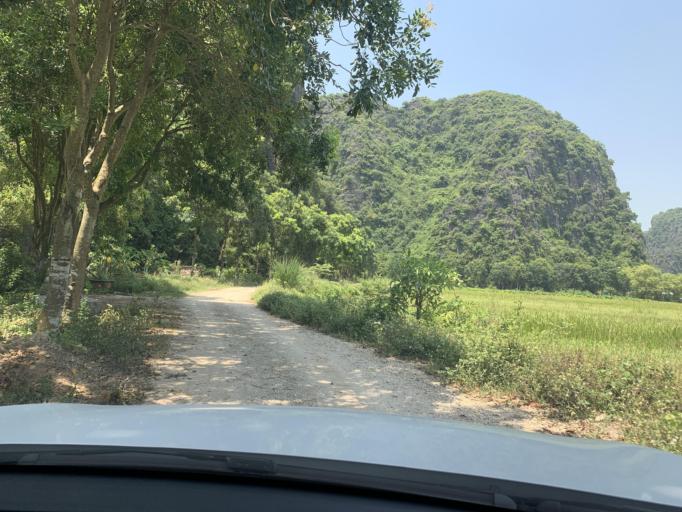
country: VN
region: Ninh Binh
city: Thanh Pho Ninh Binh
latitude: 20.2220
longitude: 105.9304
